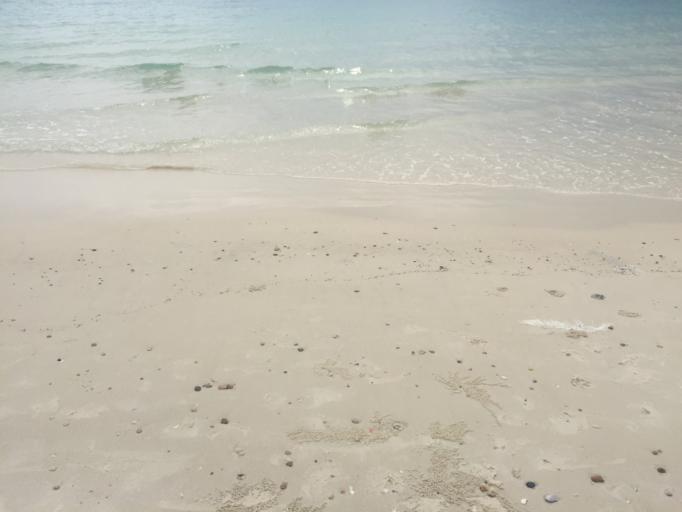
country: TH
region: Rayong
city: Rayong
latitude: 12.5641
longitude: 101.4579
